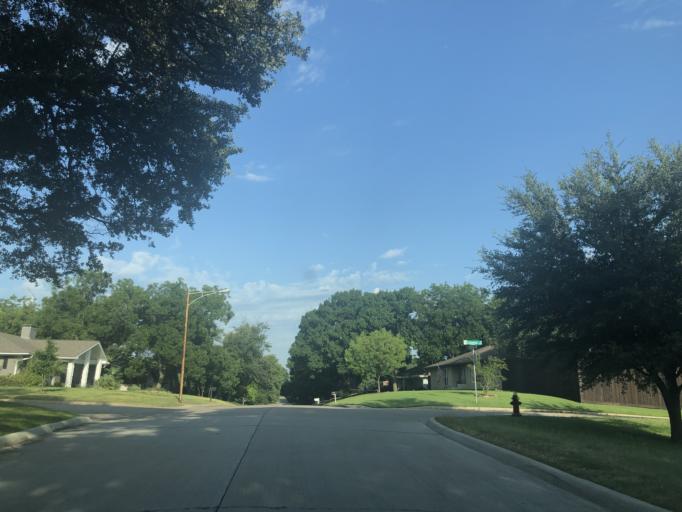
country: US
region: Texas
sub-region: Dallas County
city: Grand Prairie
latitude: 32.7614
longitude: -97.0232
